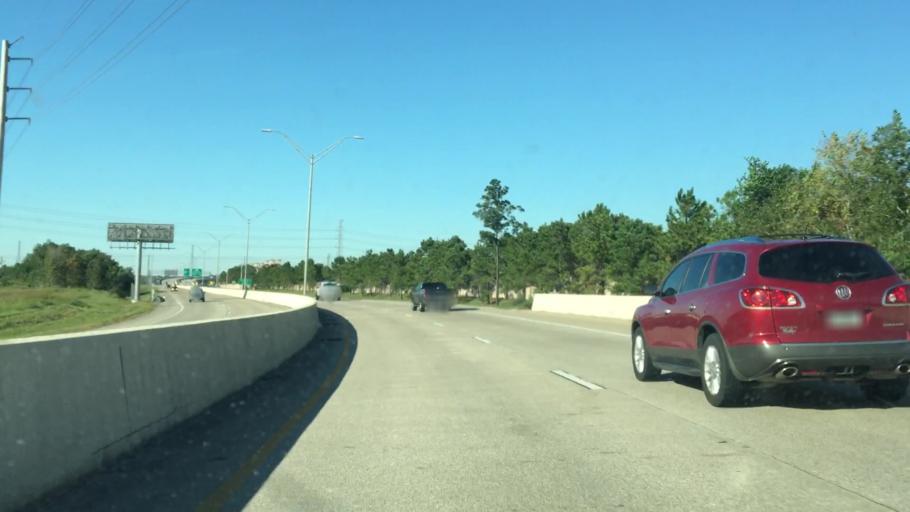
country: US
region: Texas
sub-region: Harris County
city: Webster
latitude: 29.5328
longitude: -95.1092
